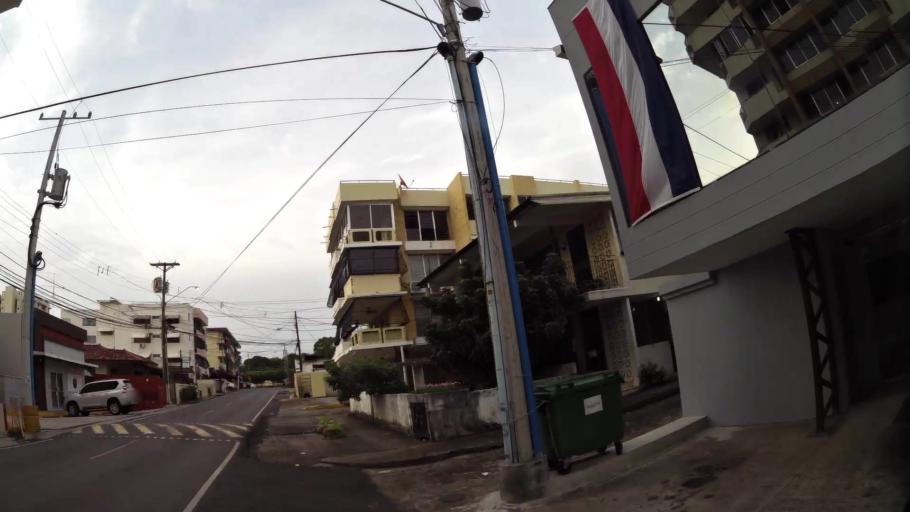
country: PA
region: Panama
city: Panama
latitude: 8.9958
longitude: -79.5085
